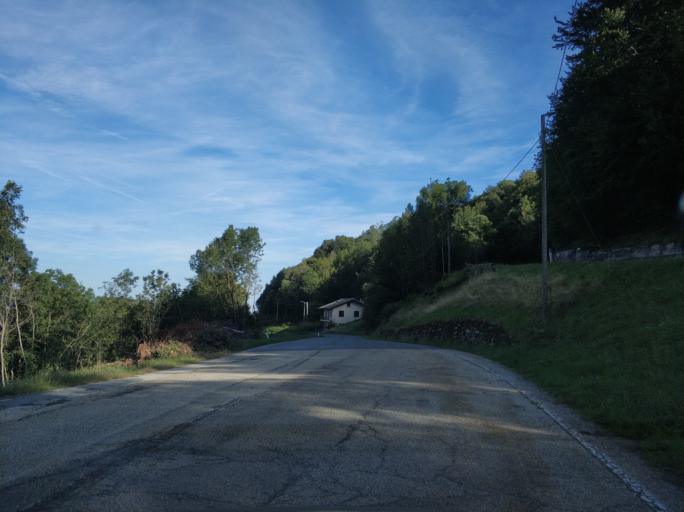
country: IT
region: Piedmont
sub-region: Provincia di Torino
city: Monastero di Lanzo
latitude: 45.3101
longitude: 7.4381
